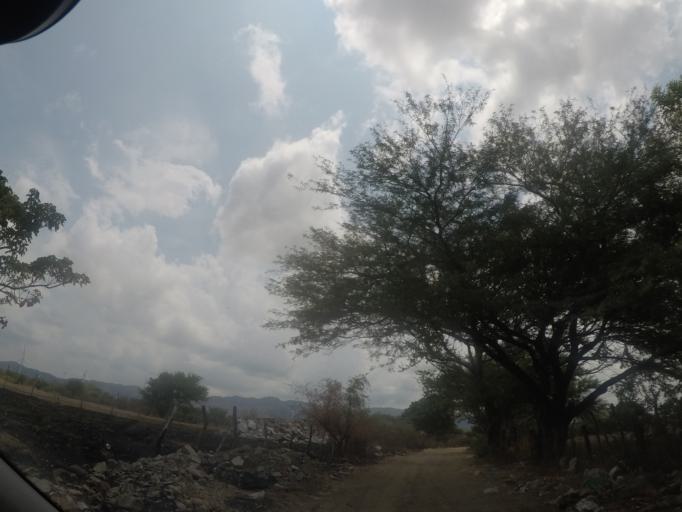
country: MX
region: Oaxaca
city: El Espinal
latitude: 16.5562
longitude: -94.9425
